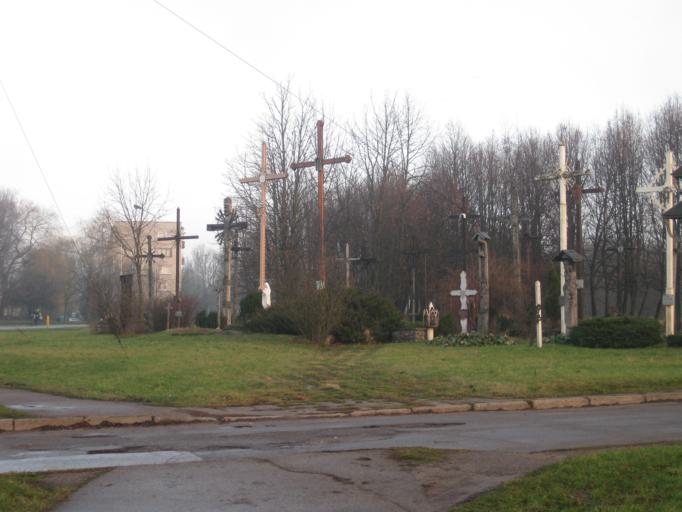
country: LT
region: Kauno apskritis
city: Dainava (Kaunas)
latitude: 54.9014
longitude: 23.9753
